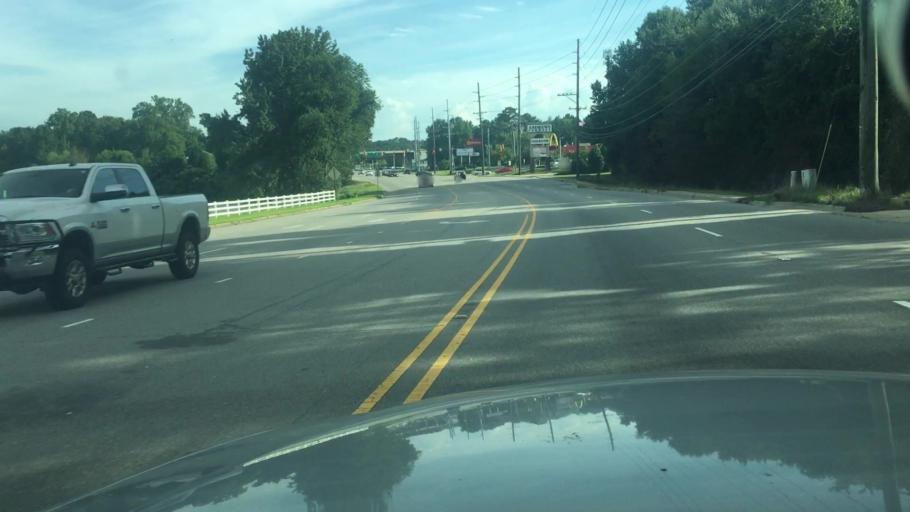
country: US
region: North Carolina
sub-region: Cumberland County
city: Eastover
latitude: 35.1594
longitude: -78.8686
